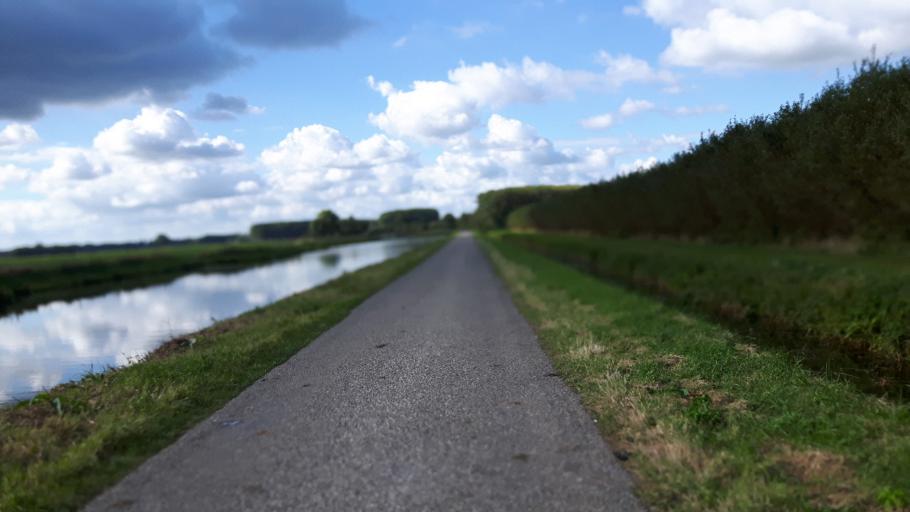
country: NL
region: South Holland
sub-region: Gemeente Leerdam
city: Leerdam
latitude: 51.9113
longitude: 5.1629
